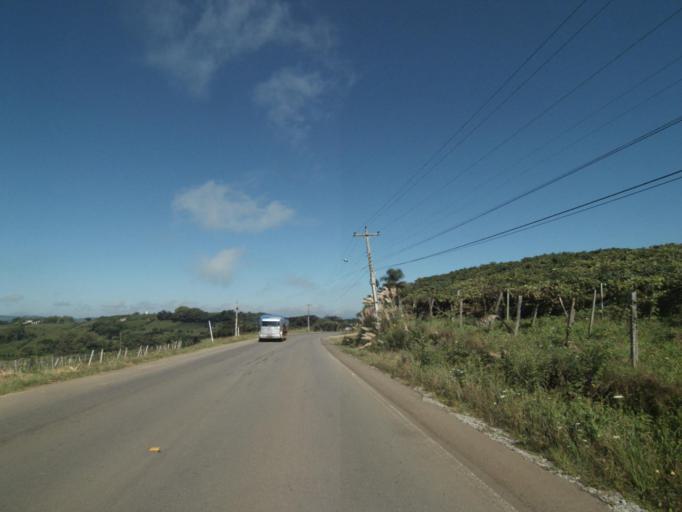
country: BR
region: Rio Grande do Sul
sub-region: Bento Goncalves
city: Bento Goncalves
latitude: -29.1154
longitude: -51.5782
